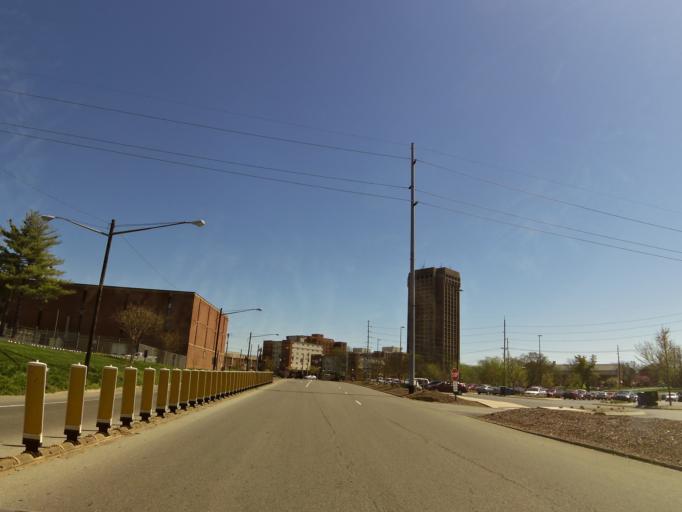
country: US
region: Kentucky
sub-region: Warren County
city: Bowling Green
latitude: 36.9814
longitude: -86.4637
